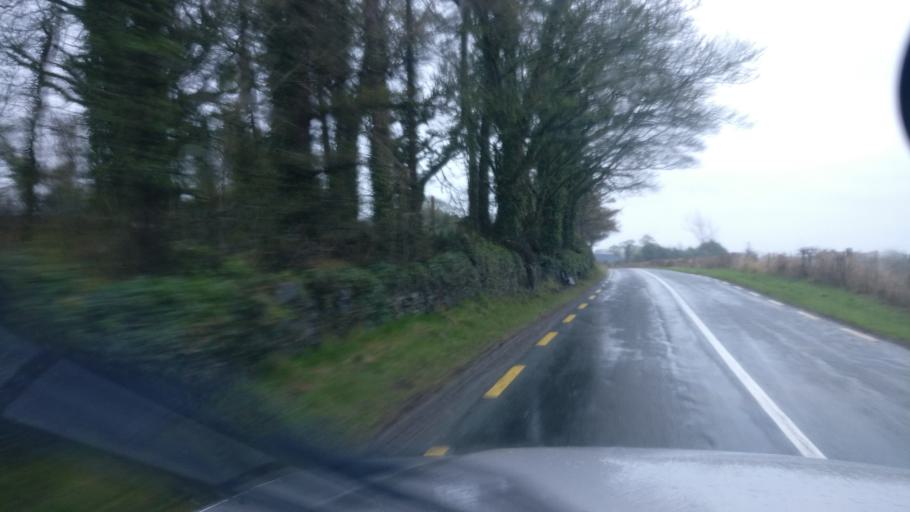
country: IE
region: Connaught
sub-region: County Galway
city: Ballinasloe
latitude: 53.2552
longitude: -8.1798
